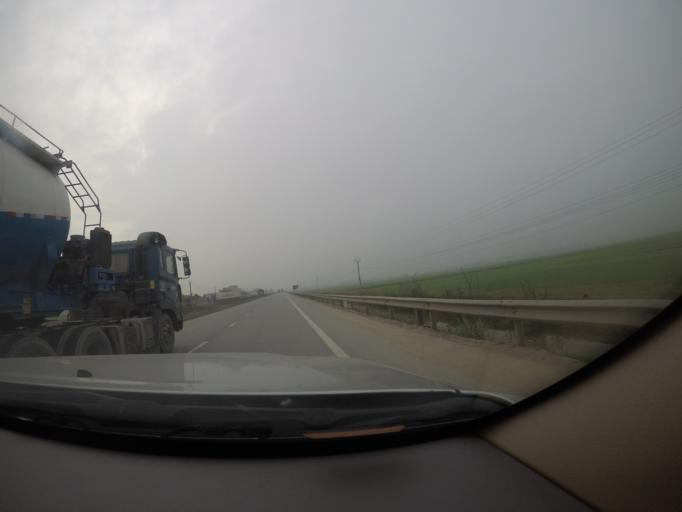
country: VN
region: Ha Tinh
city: Ky Anh
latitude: 18.1873
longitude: 106.1906
